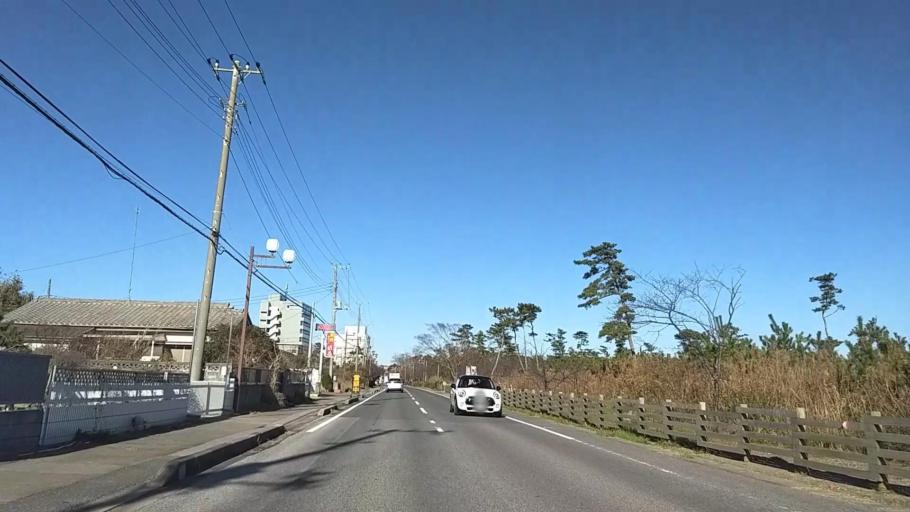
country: JP
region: Chiba
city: Mobara
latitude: 35.4261
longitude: 140.3948
